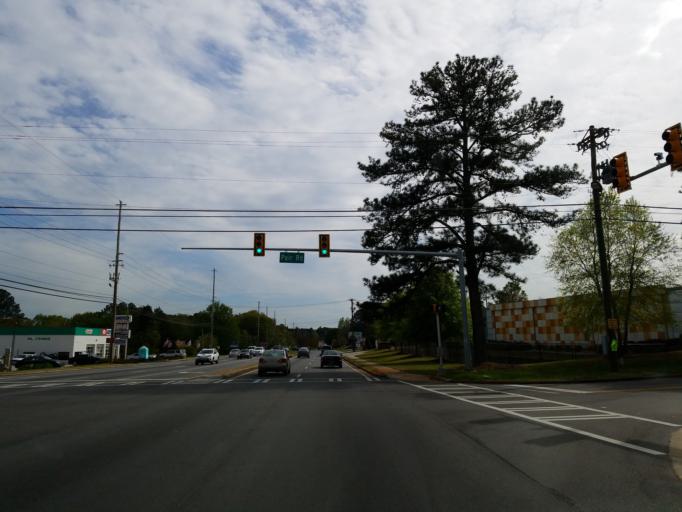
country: US
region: Georgia
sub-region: Cobb County
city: Mableton
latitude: 33.8767
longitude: -84.5897
